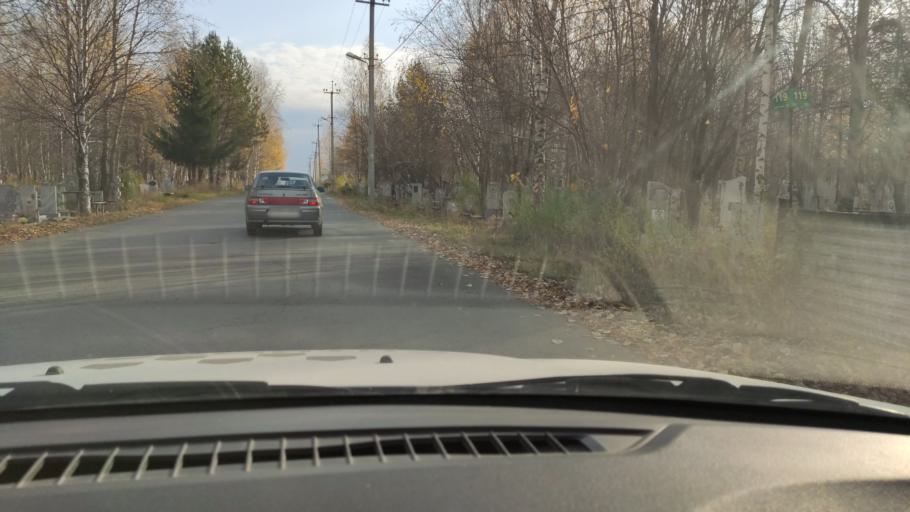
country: RU
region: Perm
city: Kondratovo
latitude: 58.0633
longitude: 56.1392
